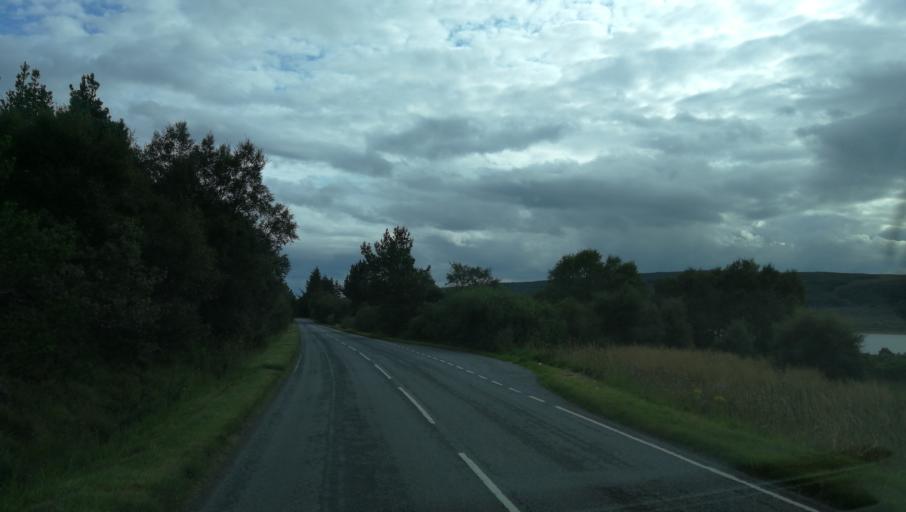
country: GB
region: Scotland
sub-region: Highland
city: Alness
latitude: 58.0429
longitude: -4.4240
